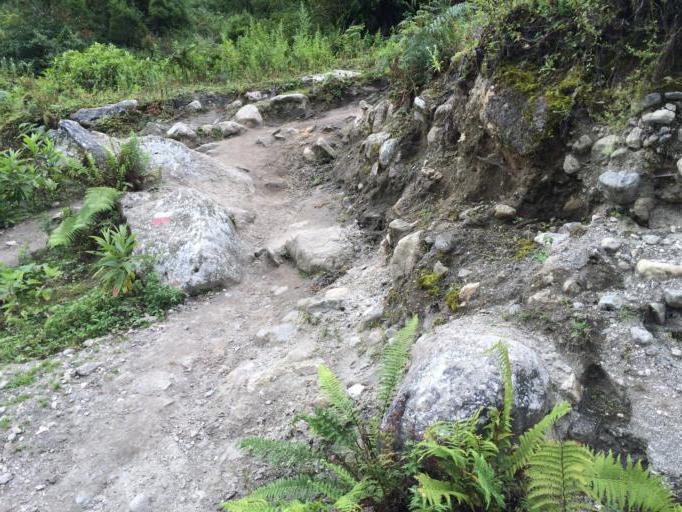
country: NP
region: Western Region
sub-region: Gandaki Zone
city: Chame
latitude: 28.5305
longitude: 84.3192
